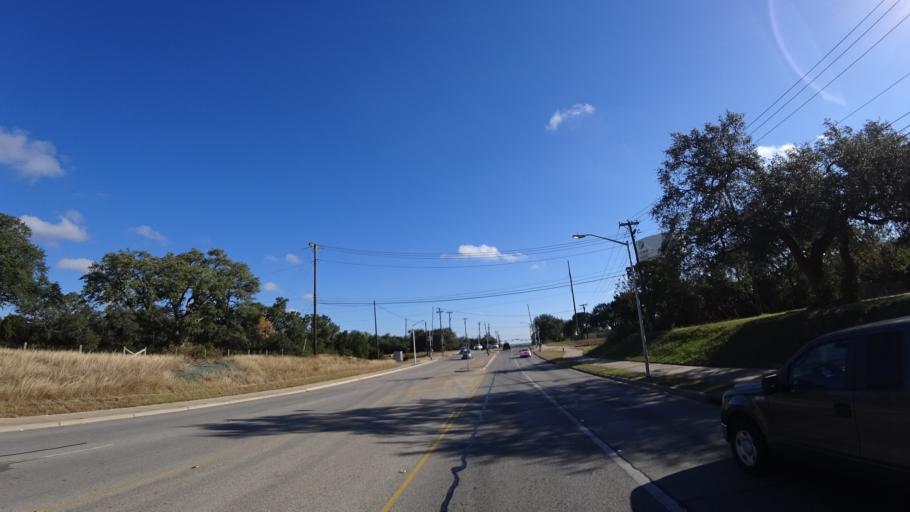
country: US
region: Texas
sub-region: Williamson County
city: Cedar Park
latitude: 30.5336
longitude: -97.8329
